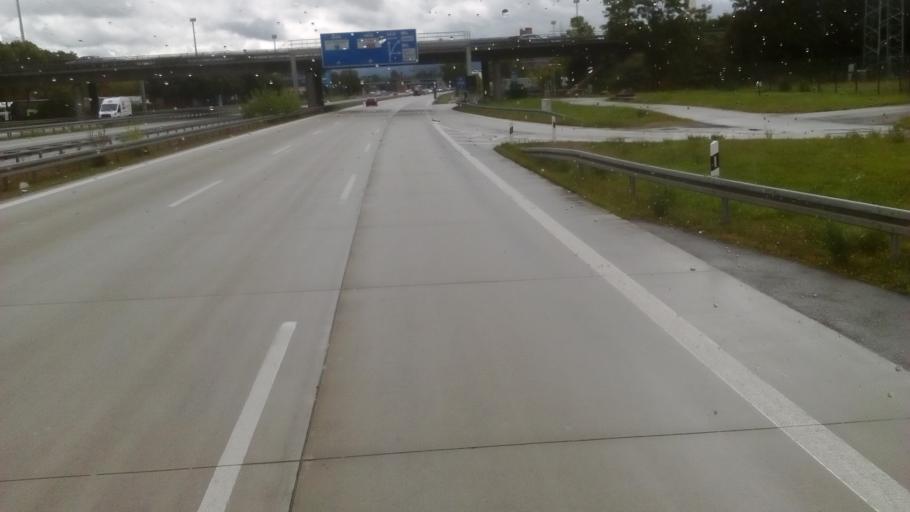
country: DE
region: Baden-Wuerttemberg
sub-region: Freiburg Region
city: Weil am Rhein
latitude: 47.6026
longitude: 7.6014
